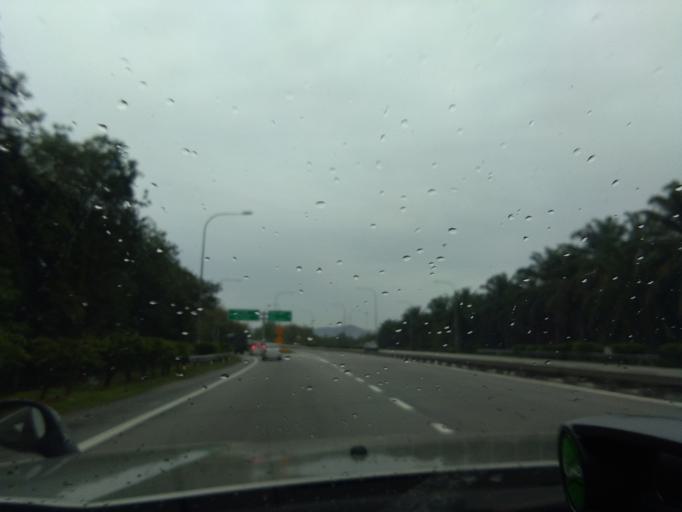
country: MY
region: Penang
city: Nibong Tebal
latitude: 5.1867
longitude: 100.4931
